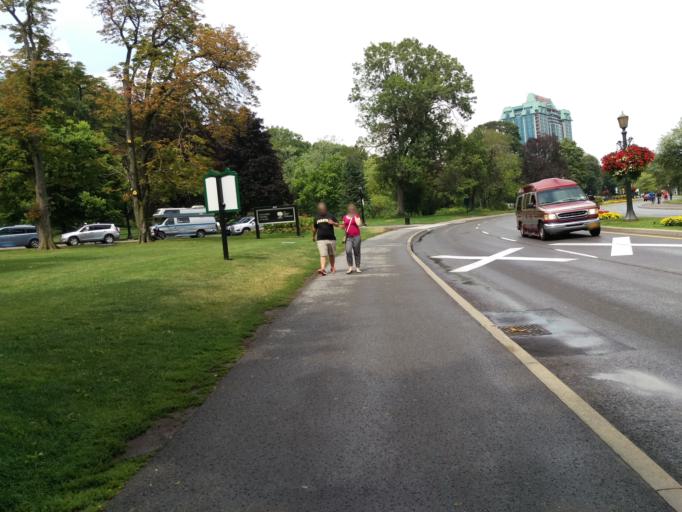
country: CA
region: Ontario
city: Niagara Falls
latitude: 43.0872
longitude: -79.0762
